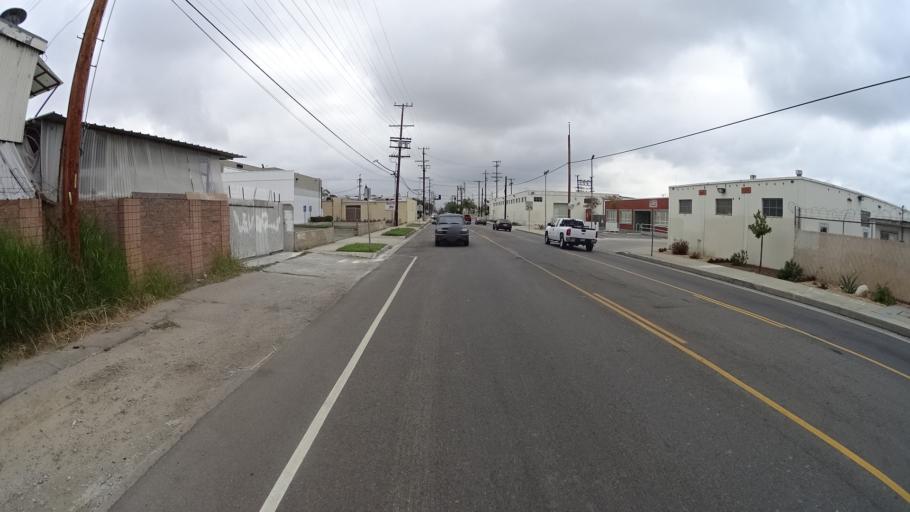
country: US
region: California
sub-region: Los Angeles County
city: Van Nuys
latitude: 34.2059
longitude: -118.4105
